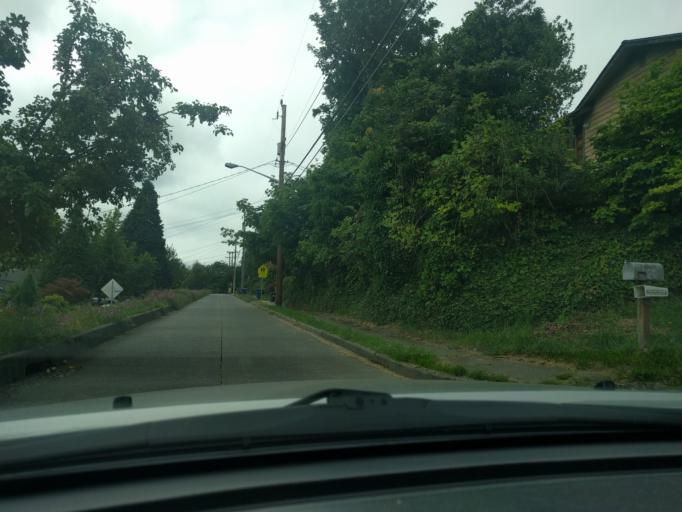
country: US
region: Washington
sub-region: King County
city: Seattle
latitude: 47.5666
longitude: -122.3602
